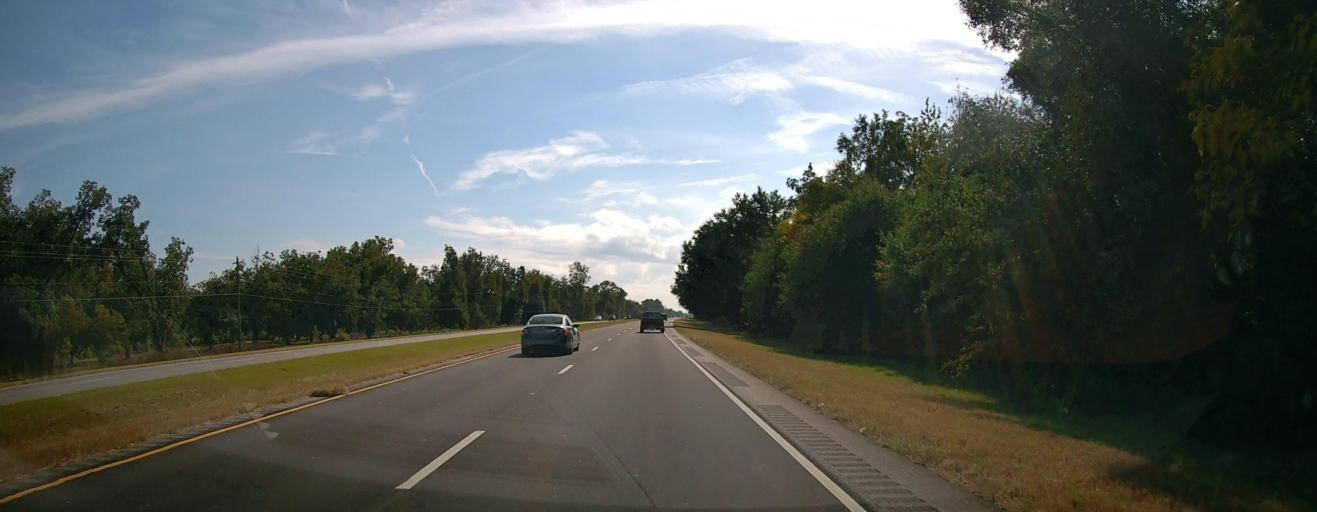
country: US
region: Georgia
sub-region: Dougherty County
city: Putney
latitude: 31.3920
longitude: -84.1470
